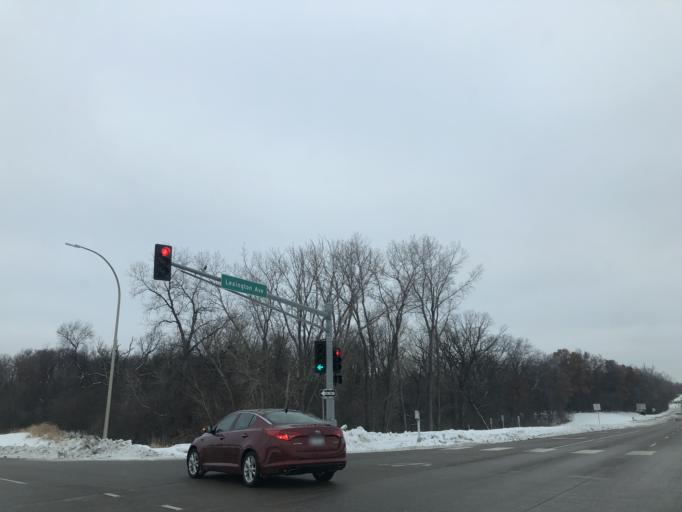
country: US
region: Minnesota
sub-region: Ramsey County
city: Arden Hills
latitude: 45.0604
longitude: -93.1472
